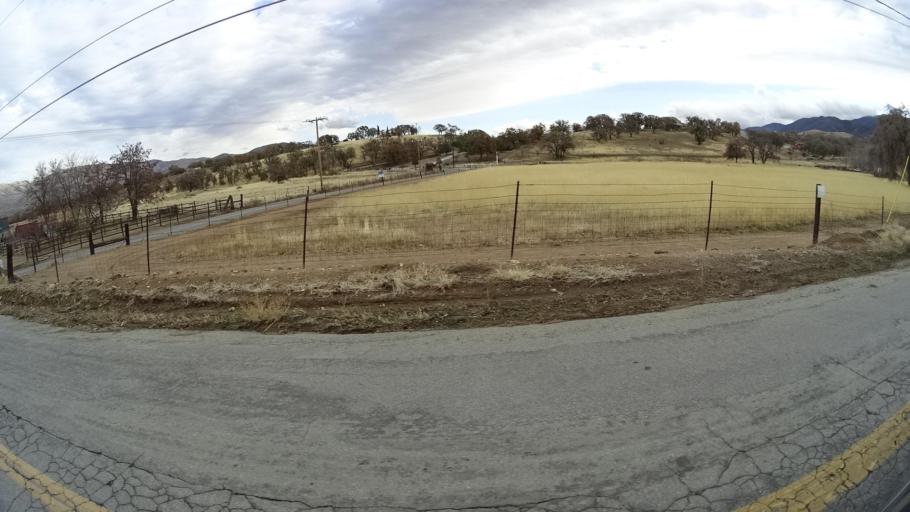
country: US
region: California
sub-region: Kern County
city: Golden Hills
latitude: 35.1287
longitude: -118.5083
